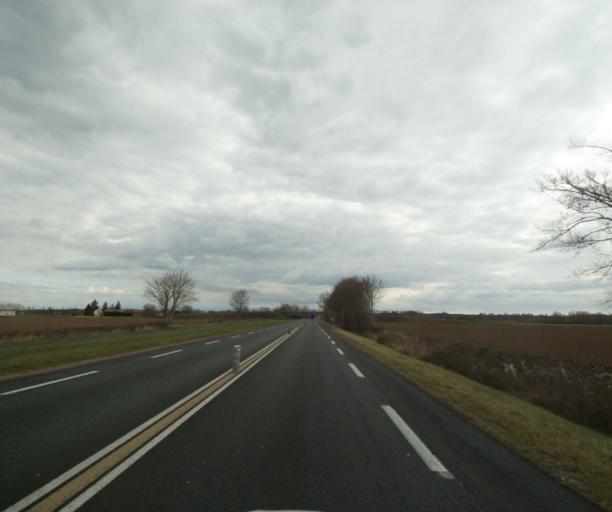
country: FR
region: Auvergne
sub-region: Departement de l'Allier
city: Toulon-sur-Allier
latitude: 46.4863
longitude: 3.3415
